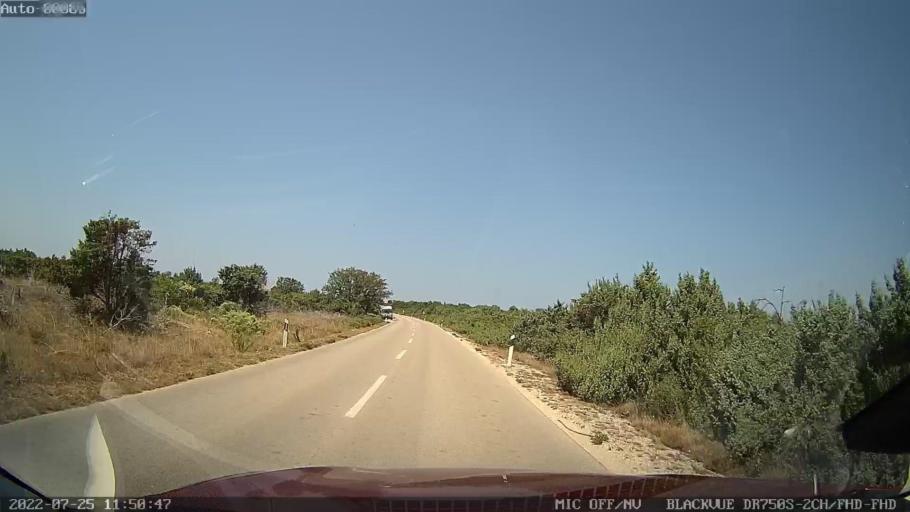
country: HR
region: Zadarska
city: Vrsi
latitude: 44.2376
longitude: 15.2604
